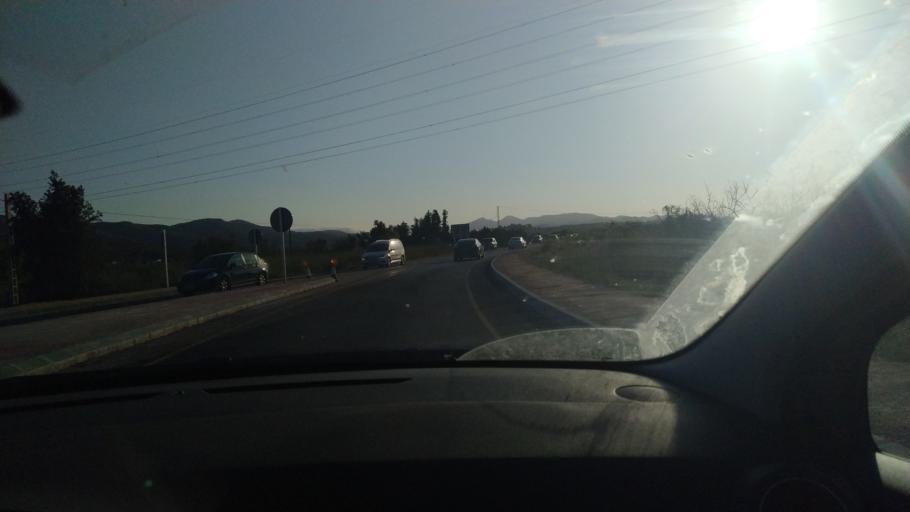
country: ES
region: Valencia
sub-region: Provincia de Alicante
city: Javea
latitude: 38.7752
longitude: 0.1303
